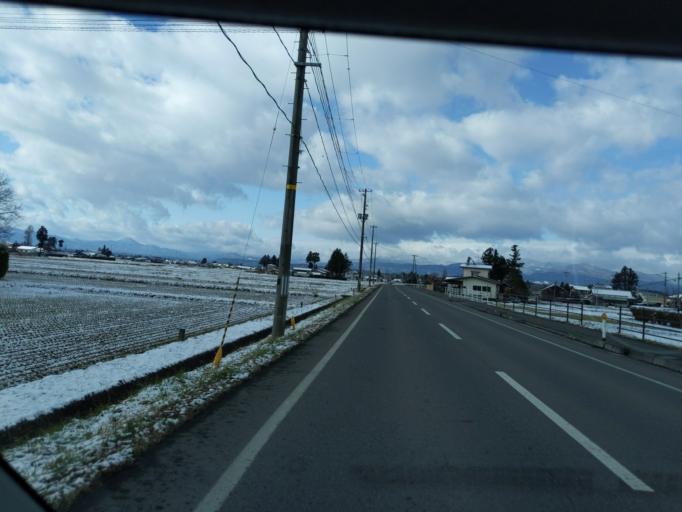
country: JP
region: Iwate
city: Mizusawa
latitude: 39.1624
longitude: 141.1085
